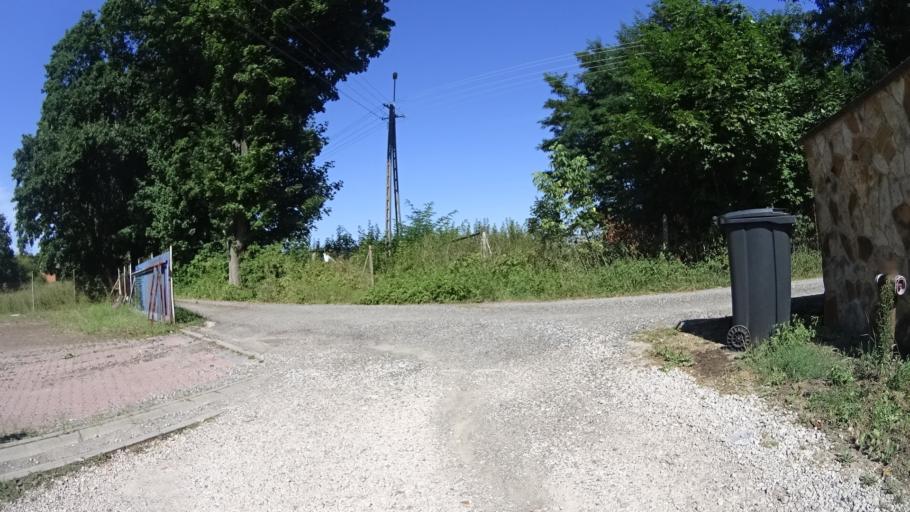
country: PL
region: Masovian Voivodeship
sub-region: Powiat bialobrzeski
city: Bialobrzegi
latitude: 51.6689
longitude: 20.9212
